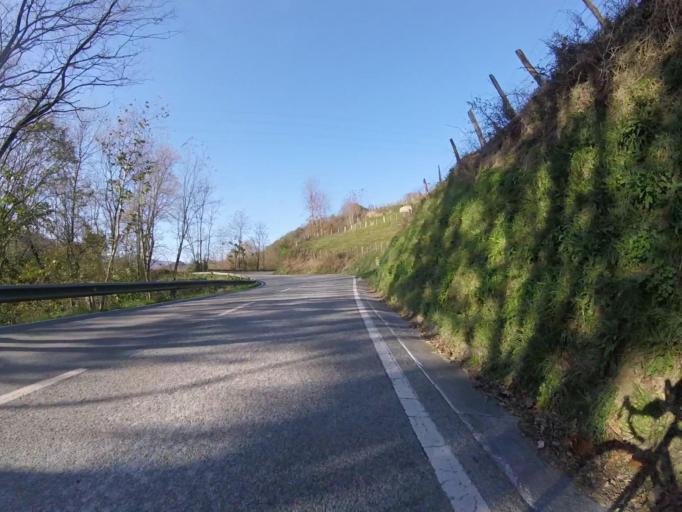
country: ES
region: Navarre
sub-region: Provincia de Navarra
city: Igantzi
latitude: 43.2261
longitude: -1.6862
